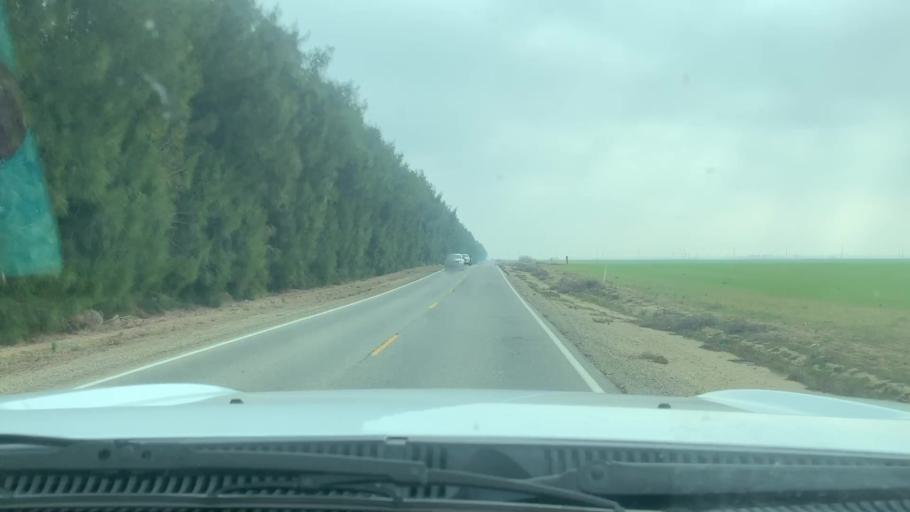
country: US
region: California
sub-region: Kern County
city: Lost Hills
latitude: 35.5106
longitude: -119.7481
